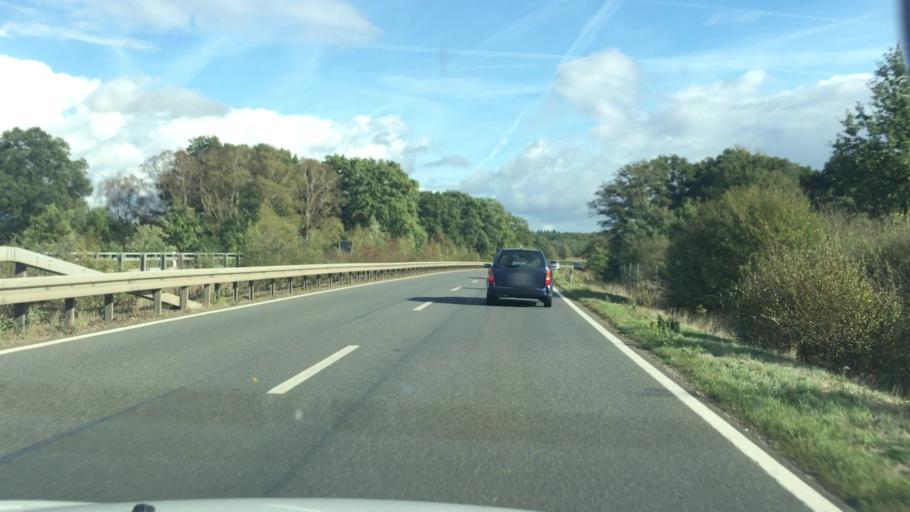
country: DE
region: Lower Saxony
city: Linsburg
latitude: 52.5780
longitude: 9.2965
